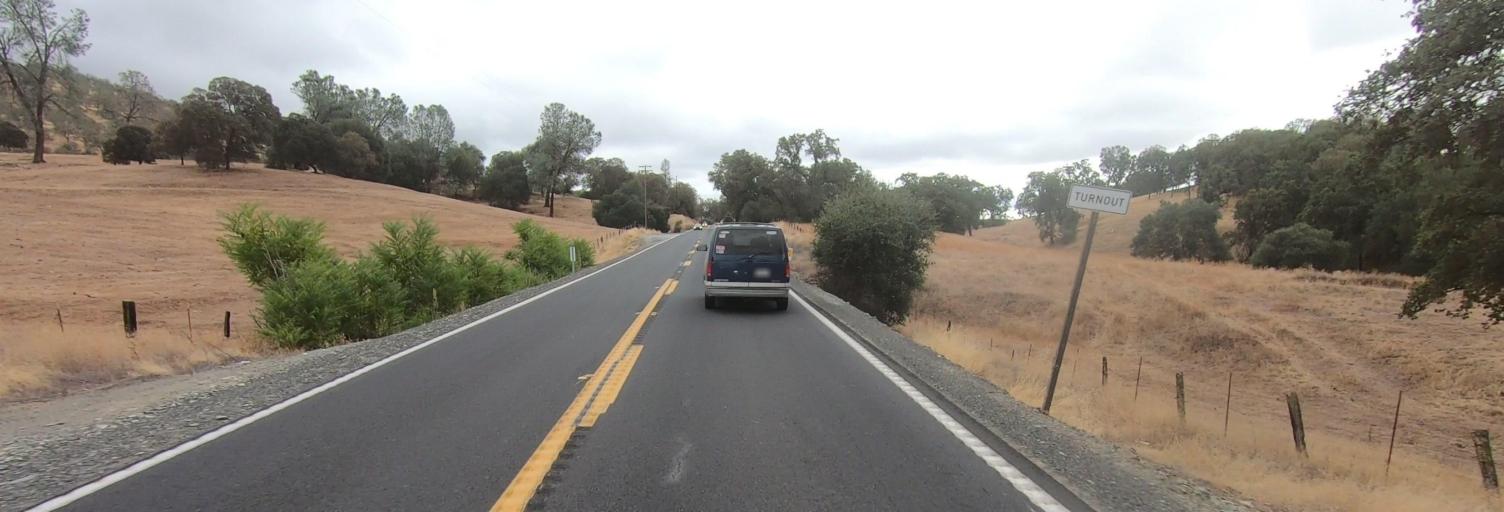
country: US
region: California
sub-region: Calaveras County
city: San Andreas
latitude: 38.1241
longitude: -120.6279
